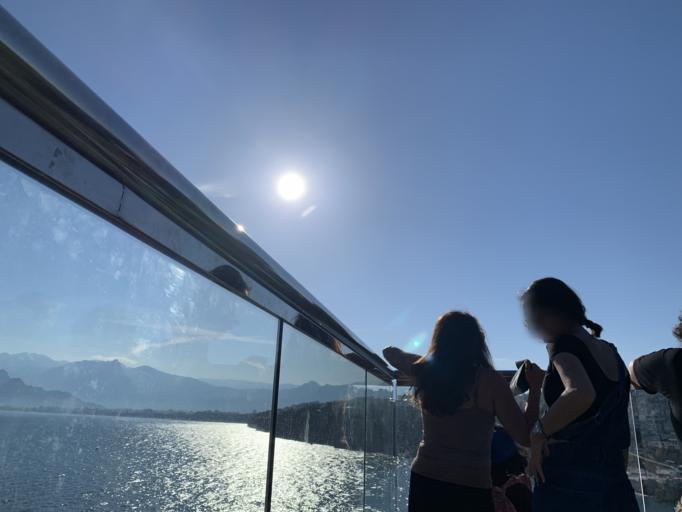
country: TR
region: Antalya
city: Antalya
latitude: 36.8829
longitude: 30.7031
